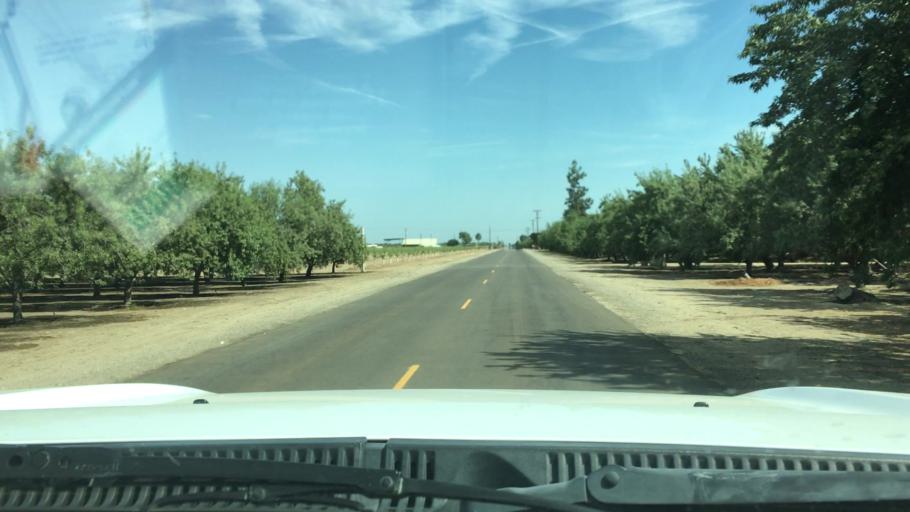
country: US
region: California
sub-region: Kern County
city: Shafter
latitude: 35.5104
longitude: -119.3500
